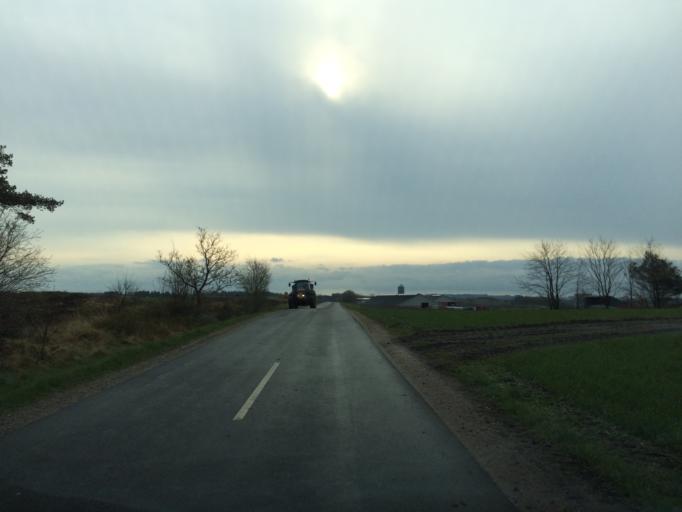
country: DK
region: Central Jutland
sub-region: Holstebro Kommune
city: Ulfborg
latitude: 56.2053
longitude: 8.4712
